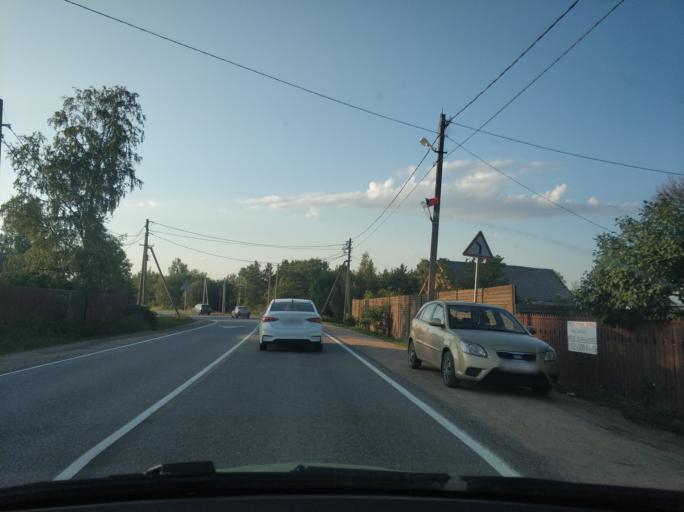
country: RU
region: Leningrad
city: Borisova Griva
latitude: 60.0891
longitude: 31.0189
